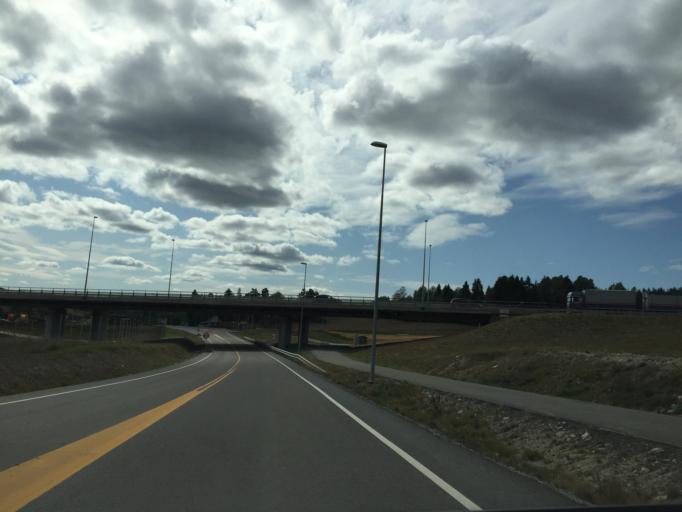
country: NO
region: Ostfold
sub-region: Hobol
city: Elvestad
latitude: 59.6294
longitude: 10.9557
